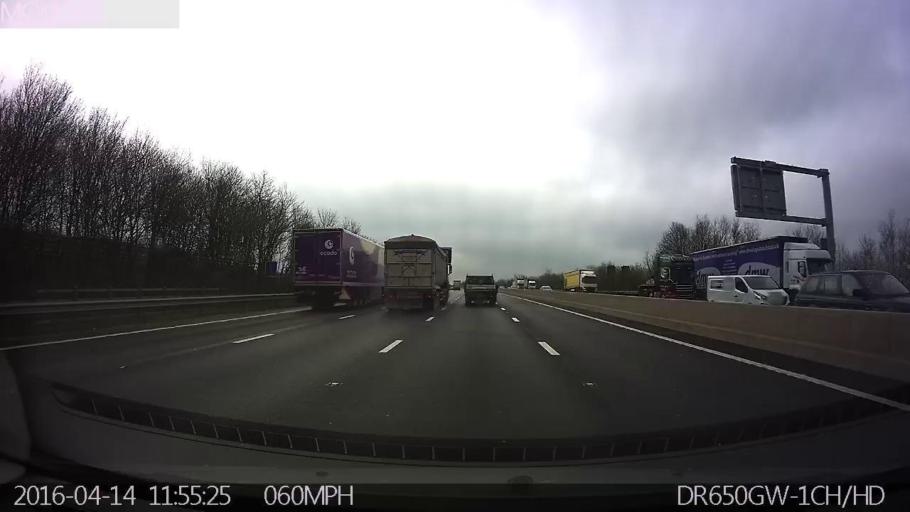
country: GB
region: England
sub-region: Derbyshire
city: Tibshelf
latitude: 53.1451
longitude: -1.3306
